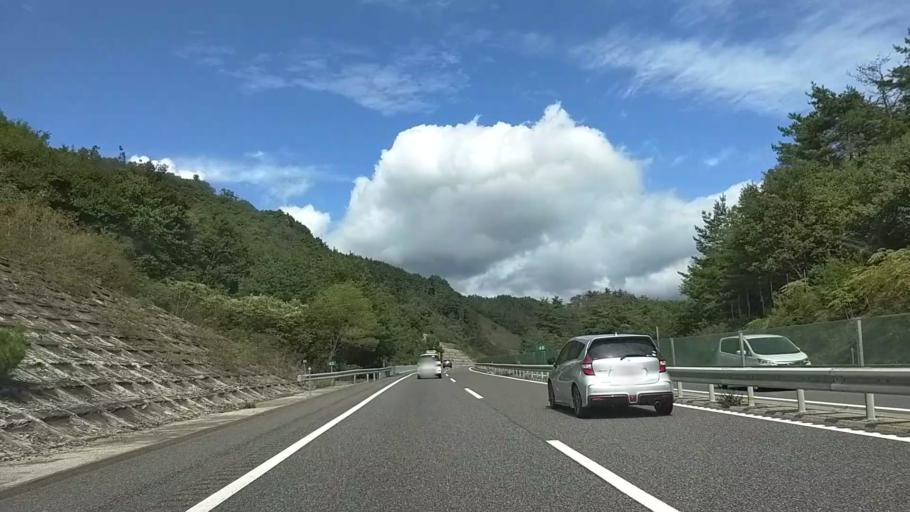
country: JP
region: Nagano
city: Hotaka
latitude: 36.4000
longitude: 138.0019
